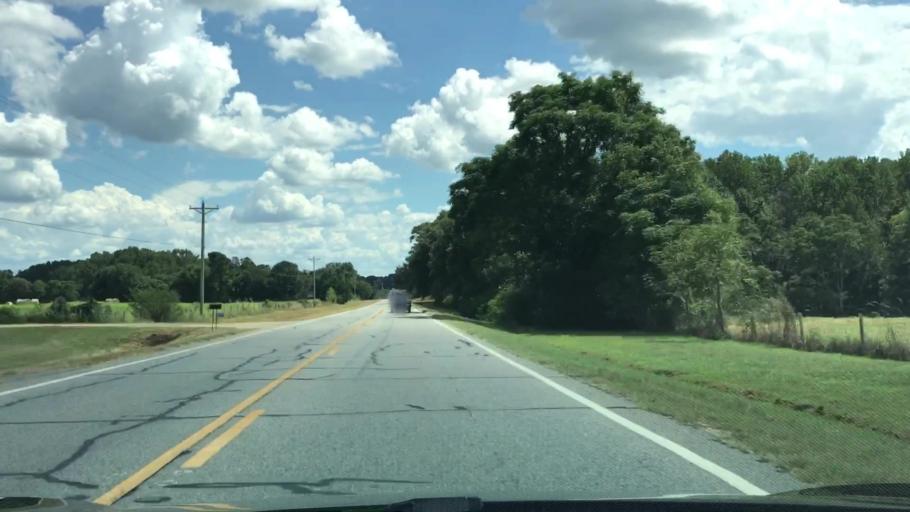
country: US
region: Georgia
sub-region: Oconee County
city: Watkinsville
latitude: 33.8238
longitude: -83.3701
